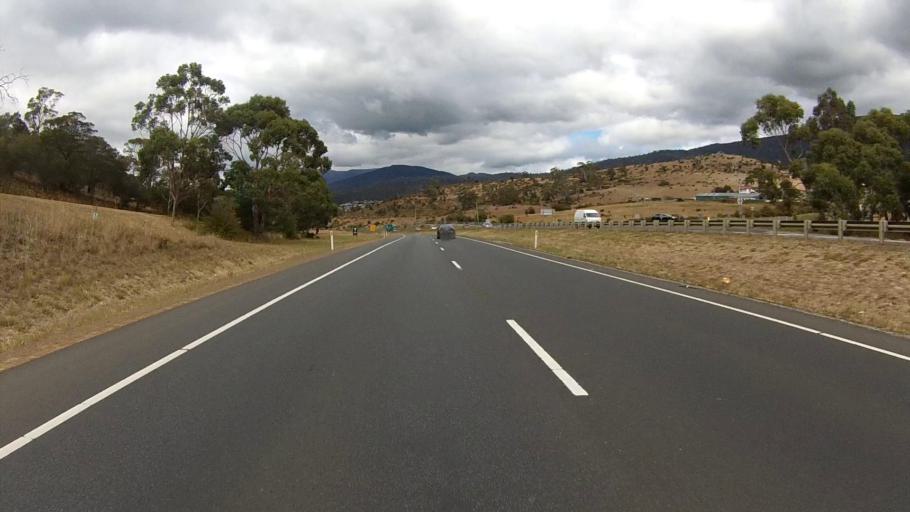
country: AU
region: Tasmania
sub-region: Glenorchy
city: Claremont
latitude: -42.7760
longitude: 147.2389
